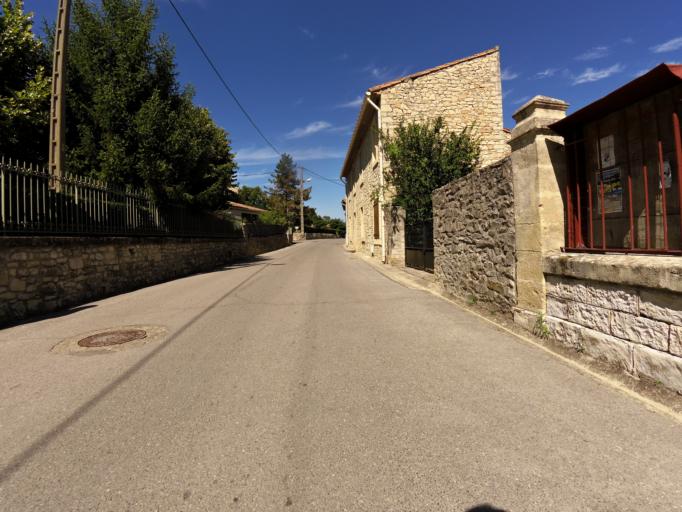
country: FR
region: Languedoc-Roussillon
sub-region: Departement du Gard
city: Quissac
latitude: 43.8736
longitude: 4.0420
